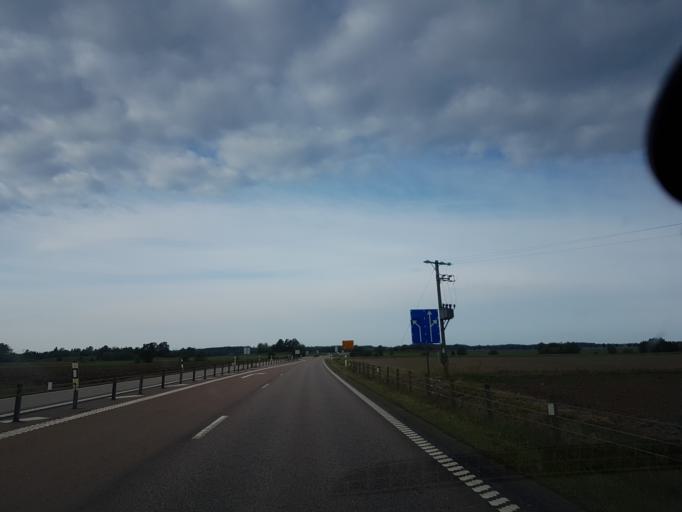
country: SE
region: OEstergoetland
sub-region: Linkopings Kommun
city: Malmslatt
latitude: 58.3812
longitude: 15.5259
